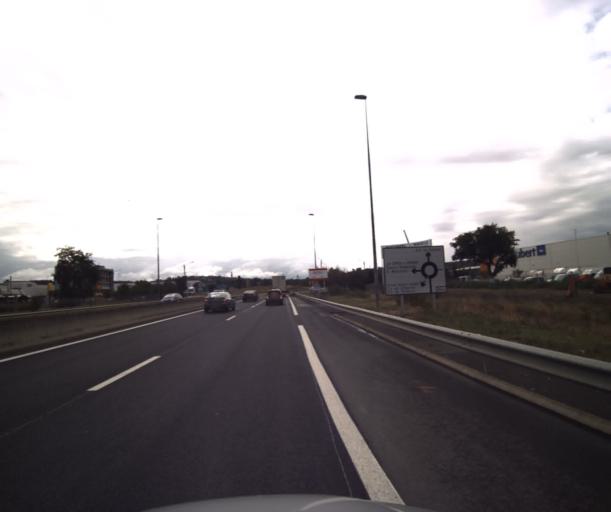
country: FR
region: Midi-Pyrenees
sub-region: Departement de la Haute-Garonne
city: Portet-sur-Garonne
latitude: 43.5493
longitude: 1.4185
